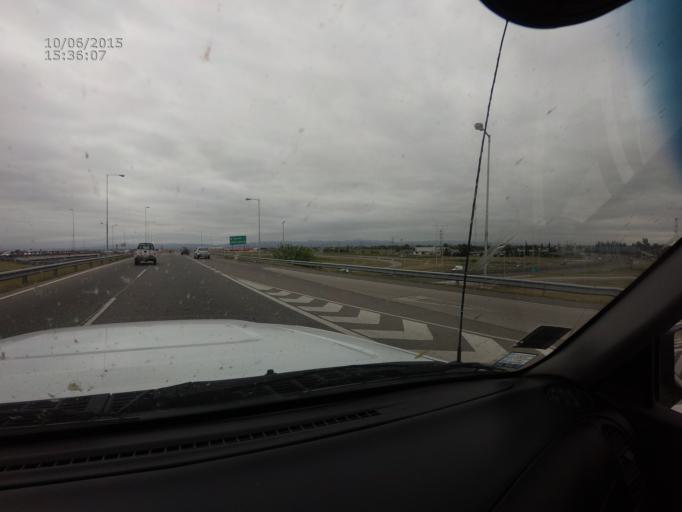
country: AR
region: Cordoba
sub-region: Departamento de Capital
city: Cordoba
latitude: -31.3539
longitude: -64.2020
